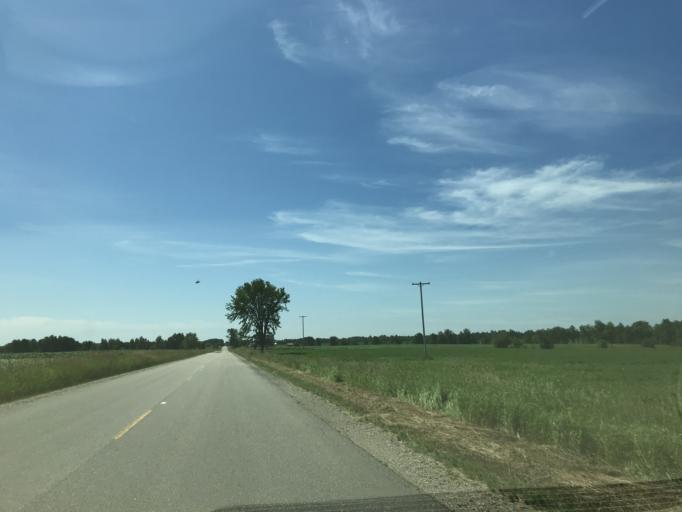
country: US
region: Michigan
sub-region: Missaukee County
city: Lake City
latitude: 44.2852
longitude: -85.0743
